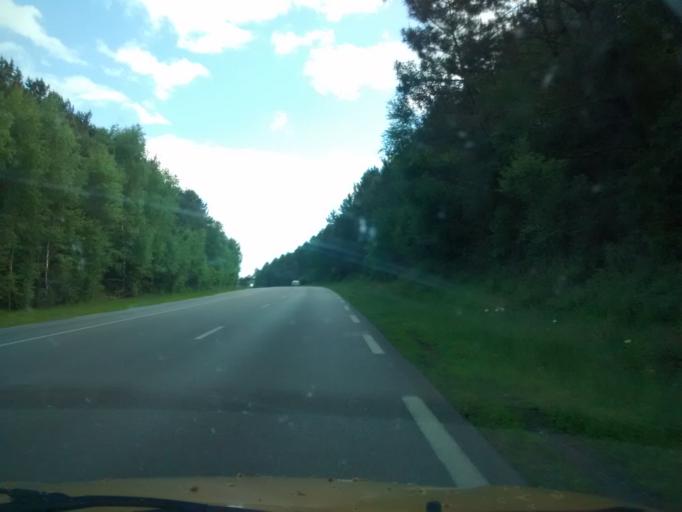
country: FR
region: Brittany
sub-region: Departement du Morbihan
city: Molac
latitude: 47.7116
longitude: -2.4433
